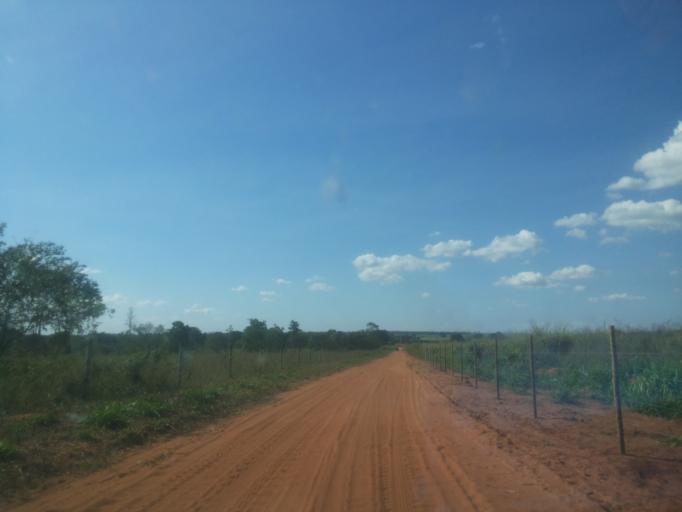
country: BR
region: Minas Gerais
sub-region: Santa Vitoria
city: Santa Vitoria
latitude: -18.9932
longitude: -50.3748
